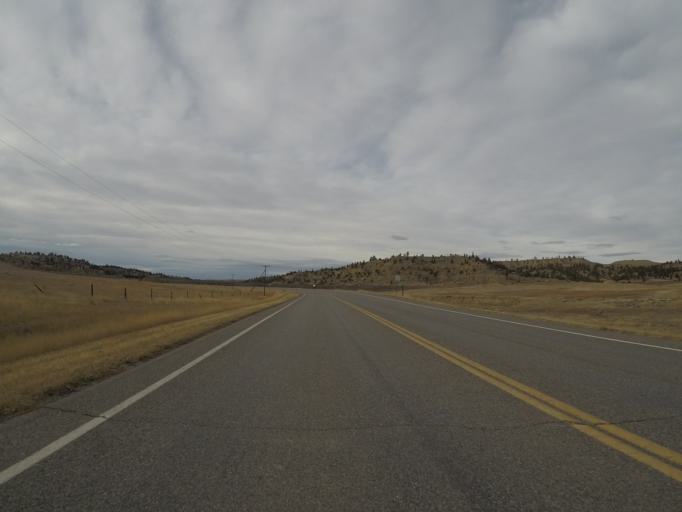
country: US
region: Montana
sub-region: Yellowstone County
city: Laurel
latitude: 45.8154
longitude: -108.6823
